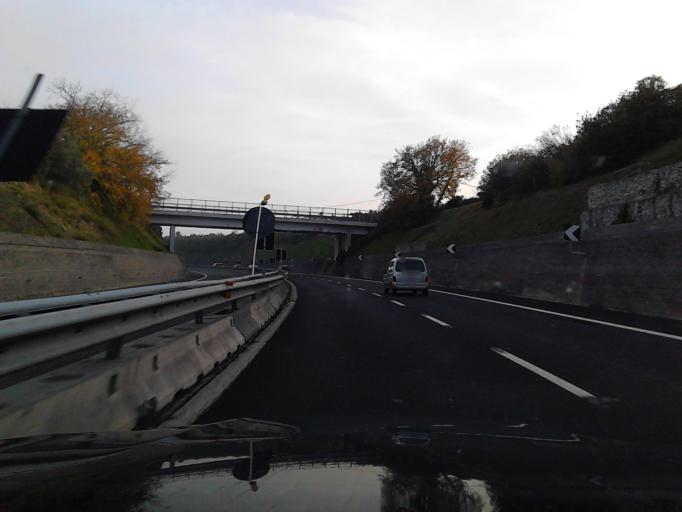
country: IT
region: Abruzzo
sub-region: Provincia di Chieti
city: San Vito Chietino
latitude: 42.3035
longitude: 14.4223
